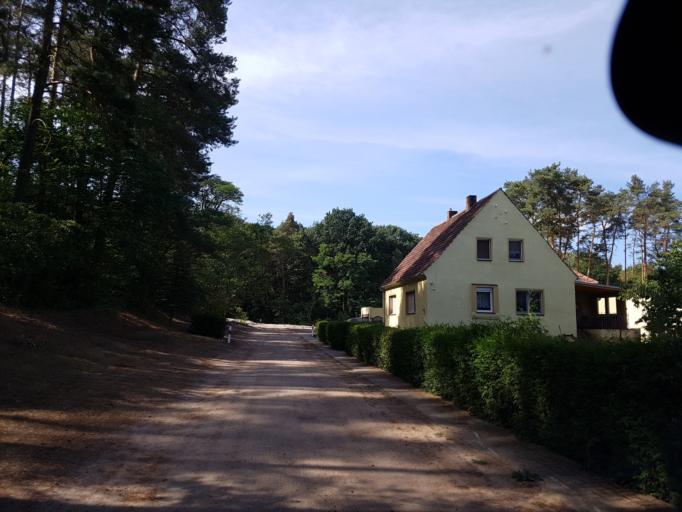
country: DE
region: Brandenburg
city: Luckau
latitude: 51.7715
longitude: 13.6838
